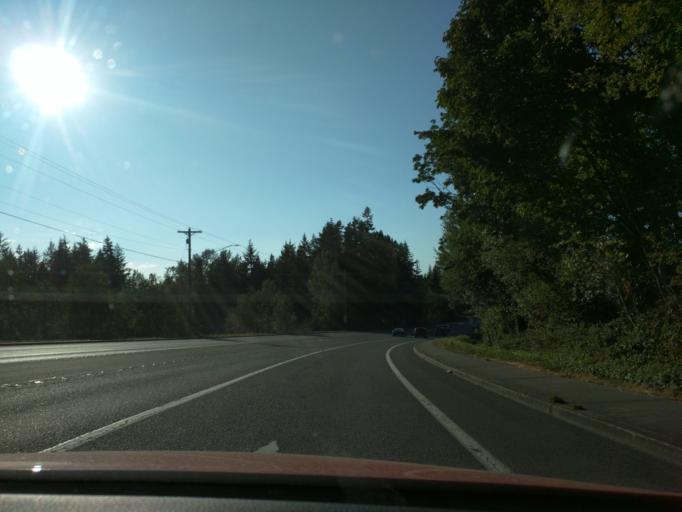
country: US
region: Washington
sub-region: Snohomish County
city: Martha Lake
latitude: 47.8826
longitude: -122.2523
